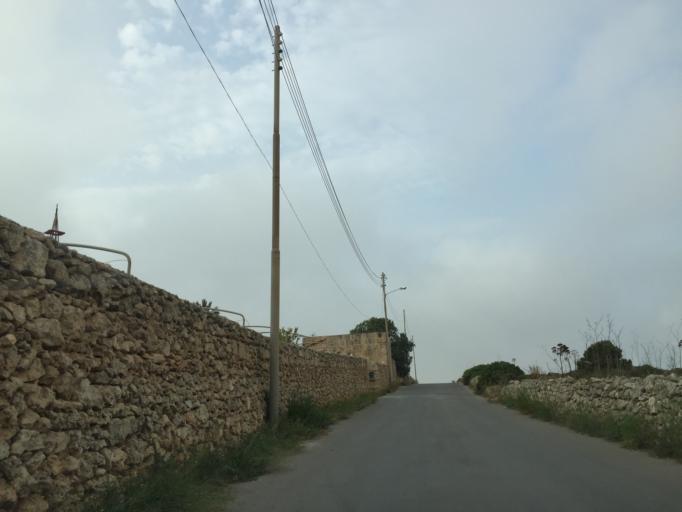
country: MT
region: L-Imgarr
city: Imgarr
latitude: 35.9349
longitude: 14.3897
